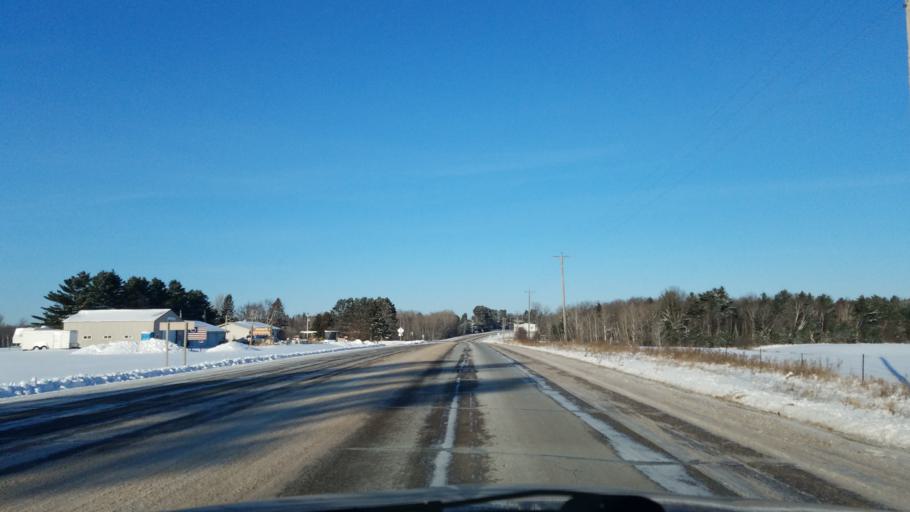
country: US
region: Wisconsin
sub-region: Barron County
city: Cumberland
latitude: 45.5185
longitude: -92.0520
